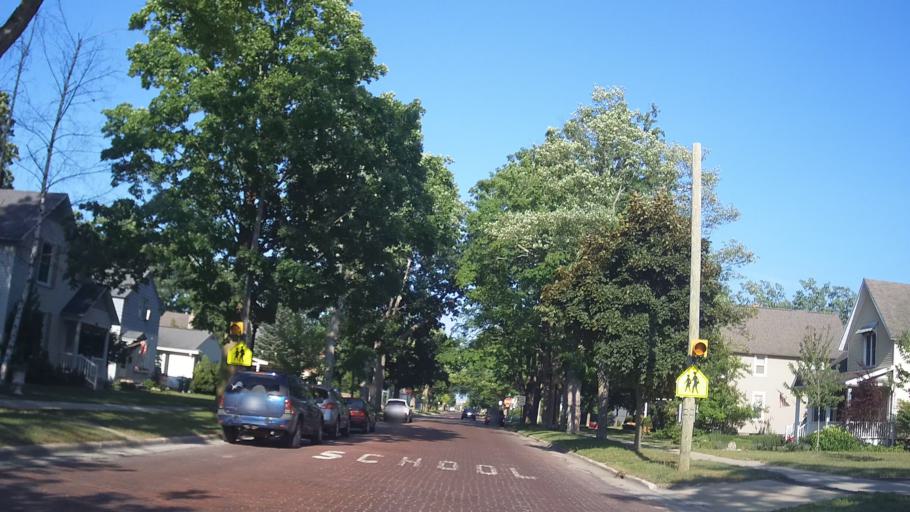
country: US
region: Michigan
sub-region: Grand Traverse County
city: Traverse City
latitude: 44.7593
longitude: -85.6297
